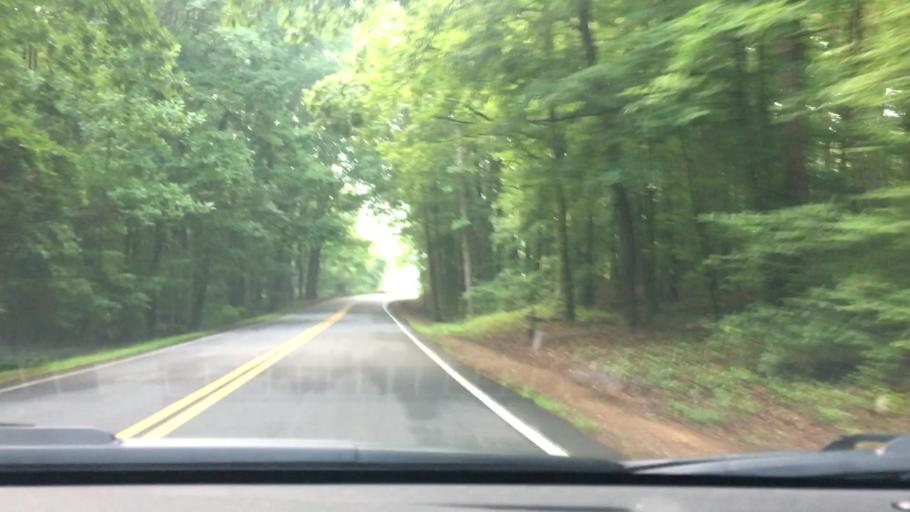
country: US
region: Georgia
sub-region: Cobb County
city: Kennesaw
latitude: 33.9877
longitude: -84.5851
